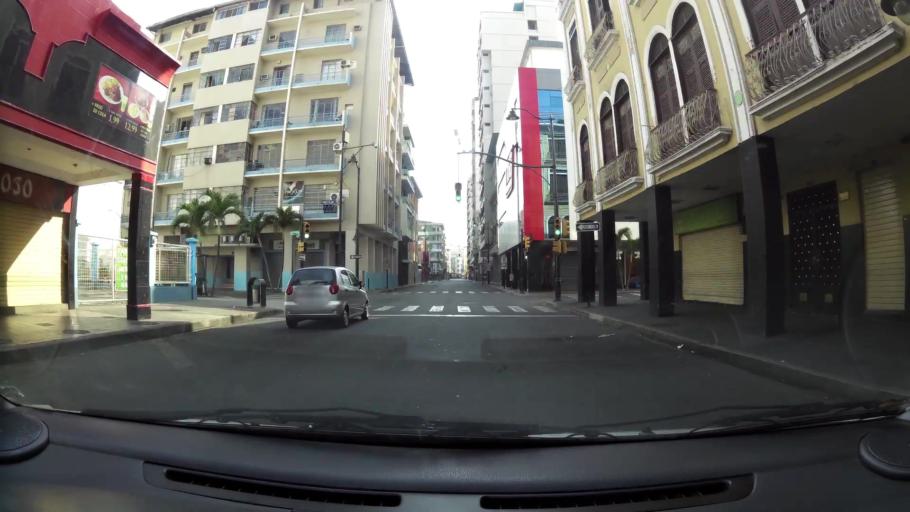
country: EC
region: Guayas
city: Guayaquil
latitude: -2.1929
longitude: -79.8832
